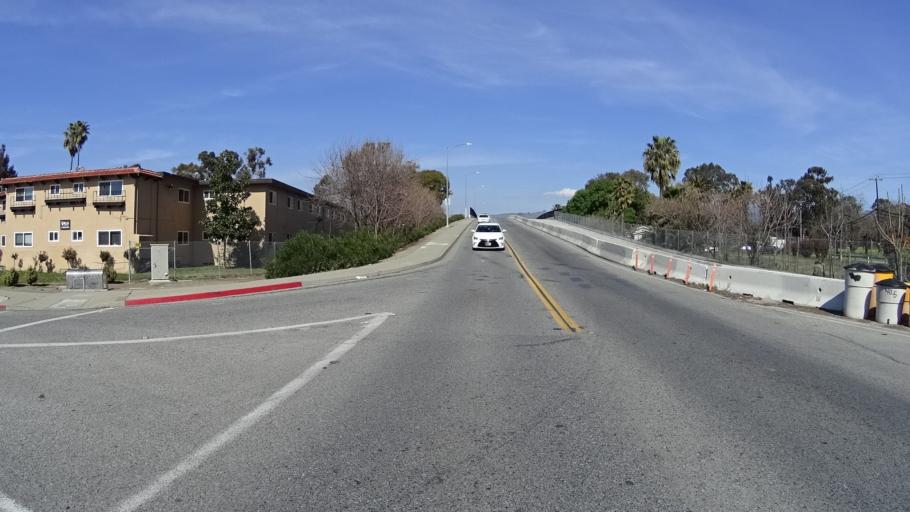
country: US
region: California
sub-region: Santa Clara County
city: San Jose
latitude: 37.3599
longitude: -121.8786
